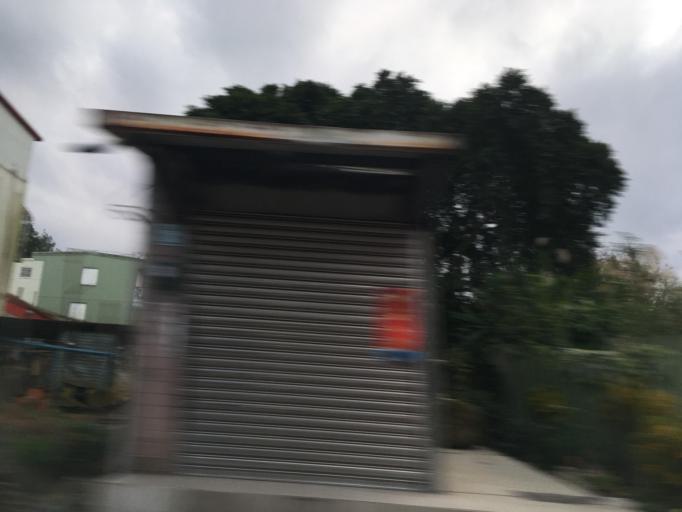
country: TW
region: Taiwan
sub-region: Yilan
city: Yilan
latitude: 24.7470
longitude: 121.7198
